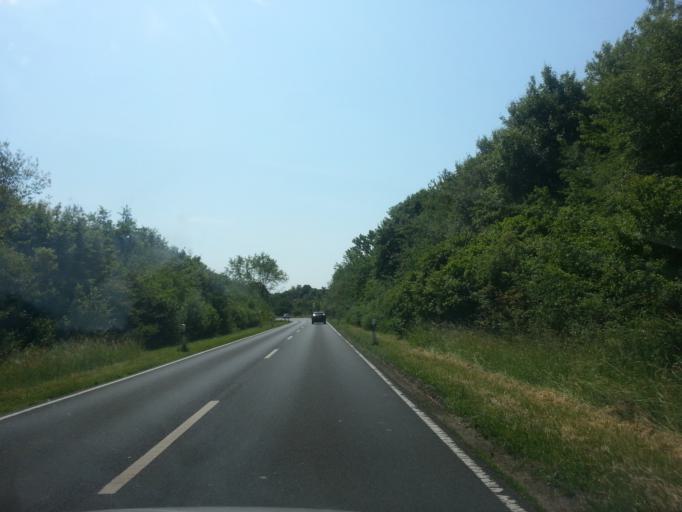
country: DE
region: Hesse
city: Dreieich
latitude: 50.0204
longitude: 8.7267
